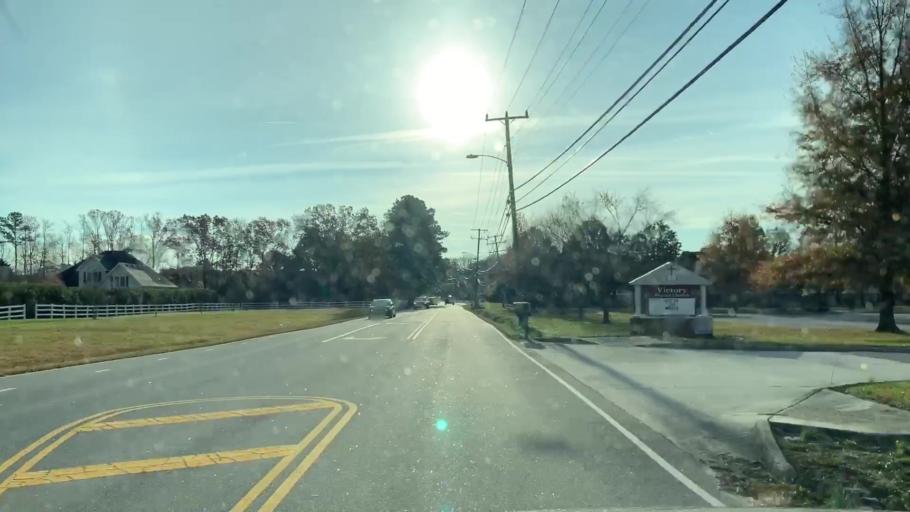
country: US
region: Virginia
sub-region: City of Chesapeake
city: Chesapeake
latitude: 36.7575
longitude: -76.1350
